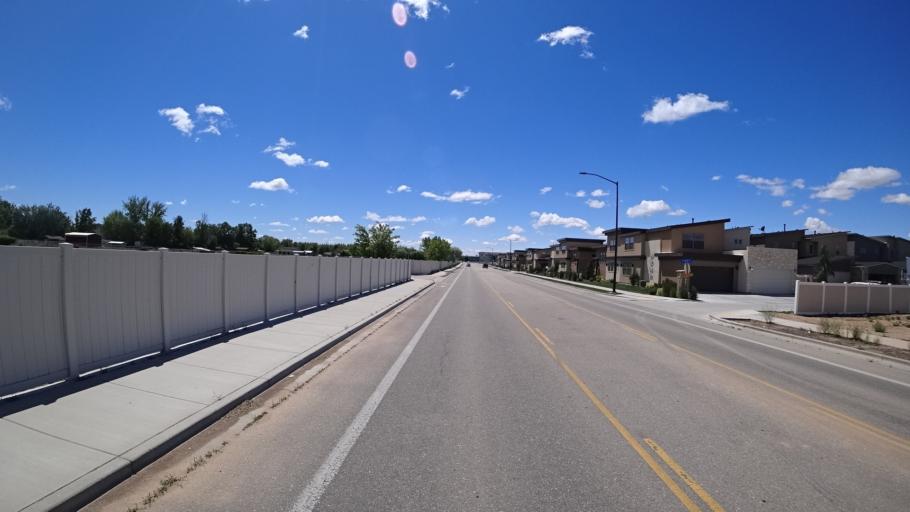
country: US
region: Idaho
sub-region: Ada County
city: Meridian
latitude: 43.6325
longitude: -116.3496
